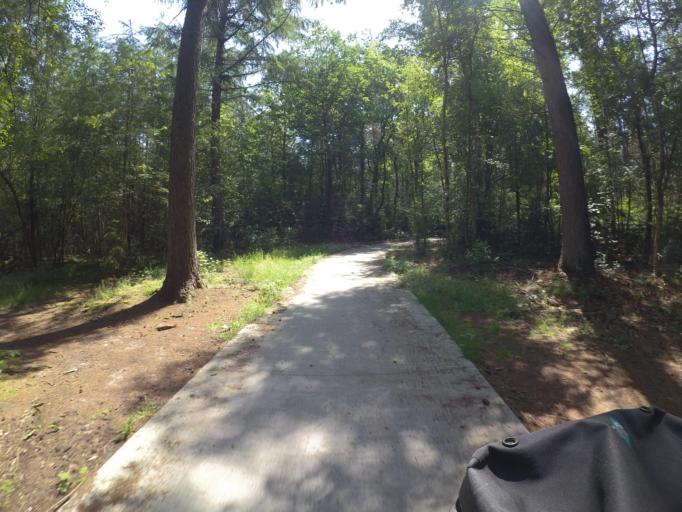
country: NL
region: Drenthe
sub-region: Gemeente De Wolden
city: Ruinen
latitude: 52.7271
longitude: 6.3578
